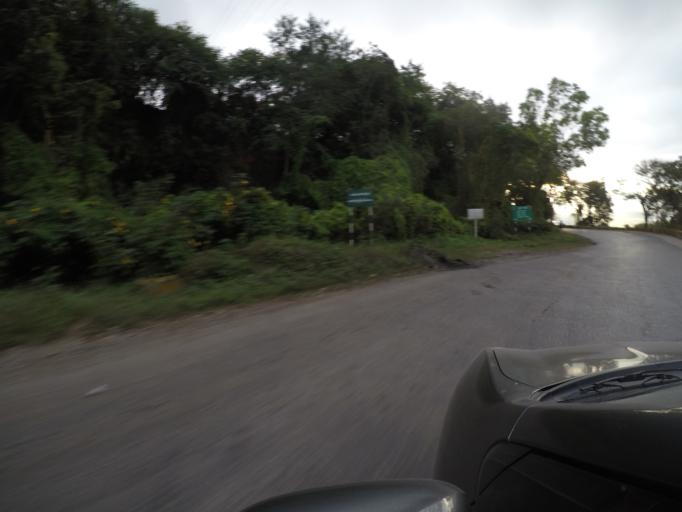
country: MM
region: Shan
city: Taunggyi
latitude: 20.8160
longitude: 97.0338
